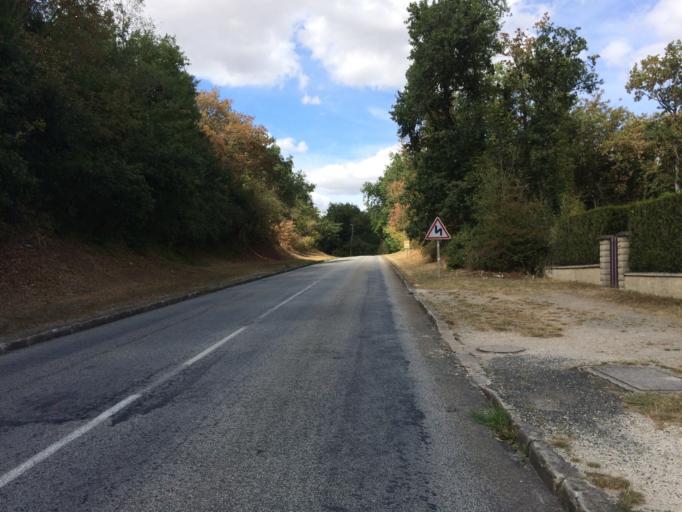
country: FR
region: Ile-de-France
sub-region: Departement de l'Essonne
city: Maisse
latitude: 48.3865
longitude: 2.3764
